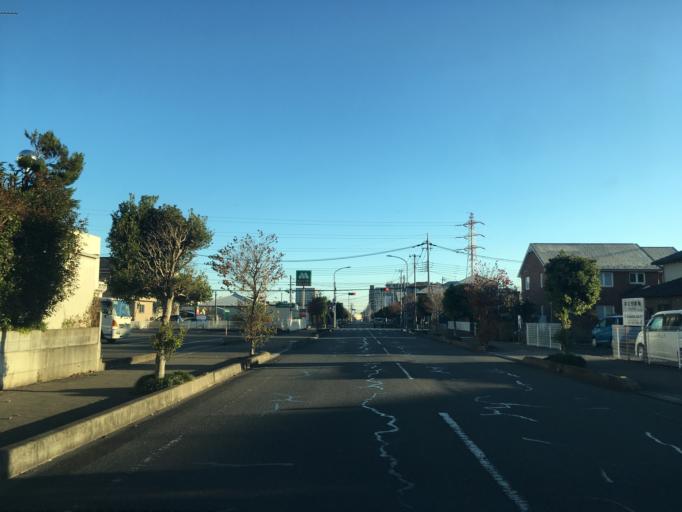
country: JP
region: Saitama
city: Sayama
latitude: 35.8161
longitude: 139.4051
